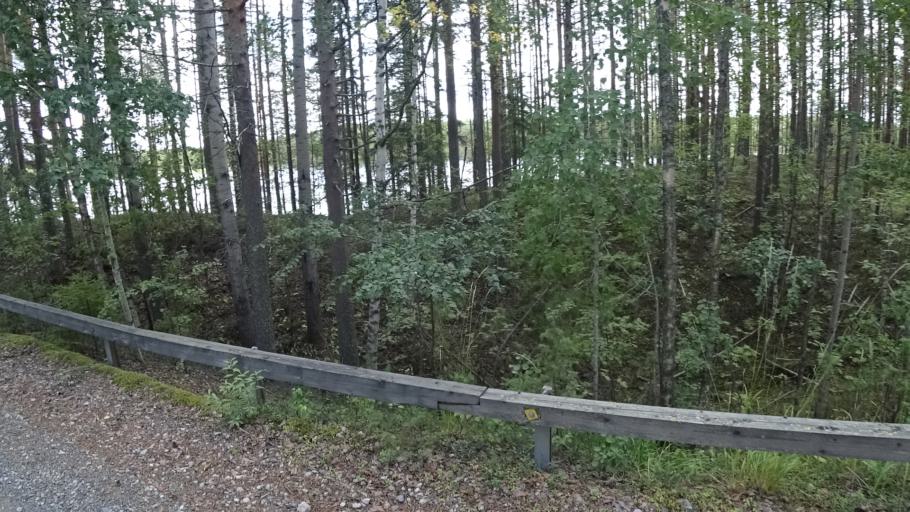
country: FI
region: North Karelia
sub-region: Joensuu
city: Ilomantsi
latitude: 62.6139
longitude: 31.1956
